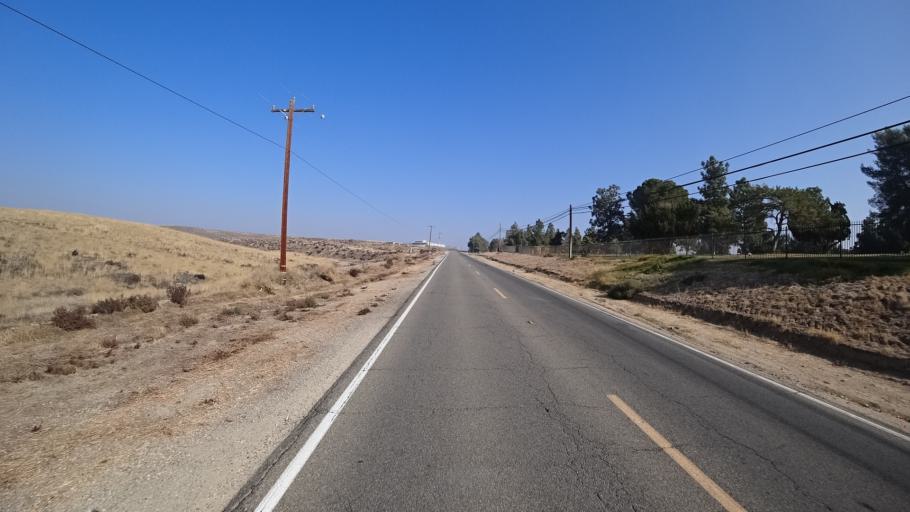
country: US
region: California
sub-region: Kern County
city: Bakersfield
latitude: 35.3808
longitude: -118.9027
